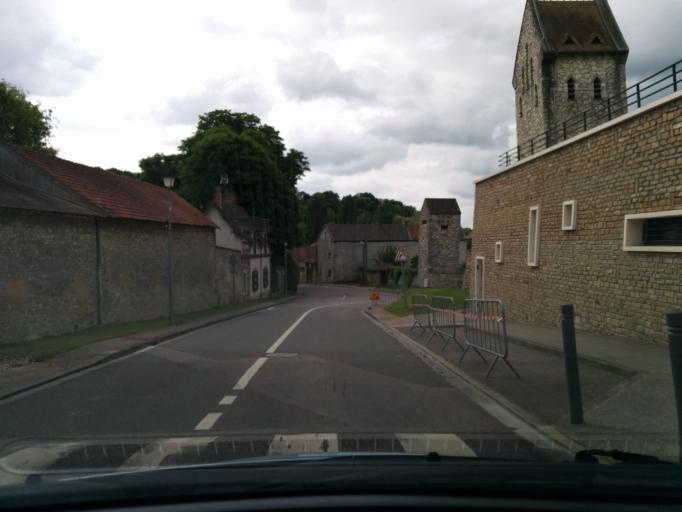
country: FR
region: Ile-de-France
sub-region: Departement des Yvelines
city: Issou
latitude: 49.0089
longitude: 1.7789
